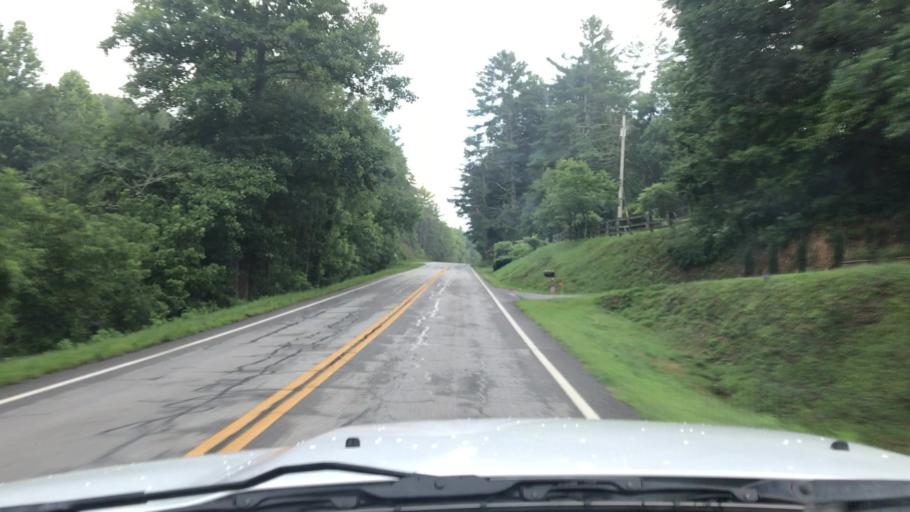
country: US
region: Georgia
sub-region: Fannin County
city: Blue Ridge
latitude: 34.9402
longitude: -84.2502
